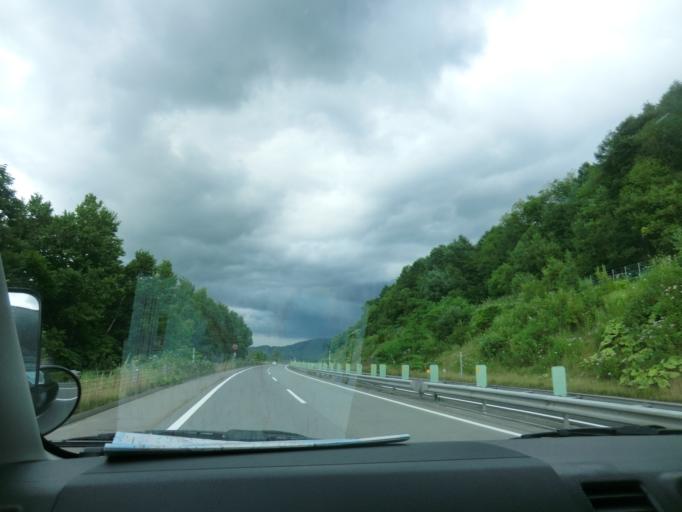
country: JP
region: Hokkaido
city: Fukagawa
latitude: 43.7102
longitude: 142.1491
